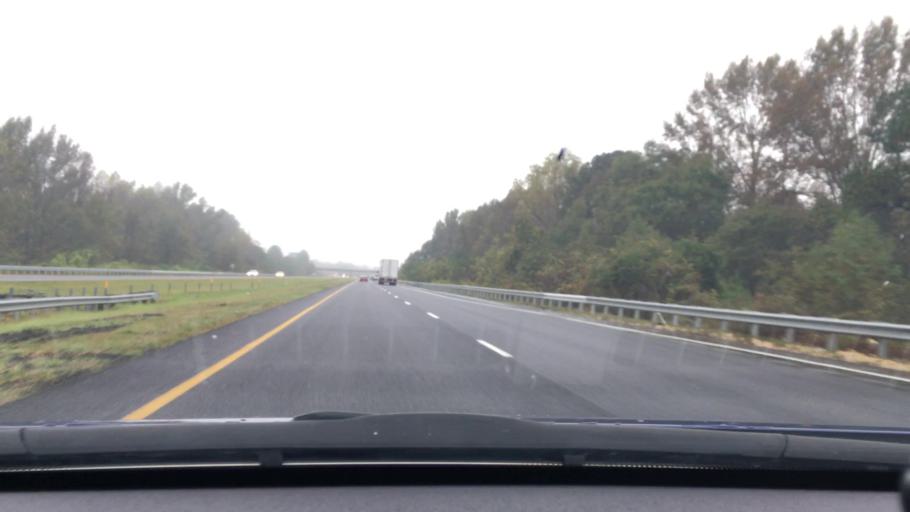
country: US
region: South Carolina
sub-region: Florence County
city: Timmonsville
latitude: 34.2029
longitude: -80.0619
